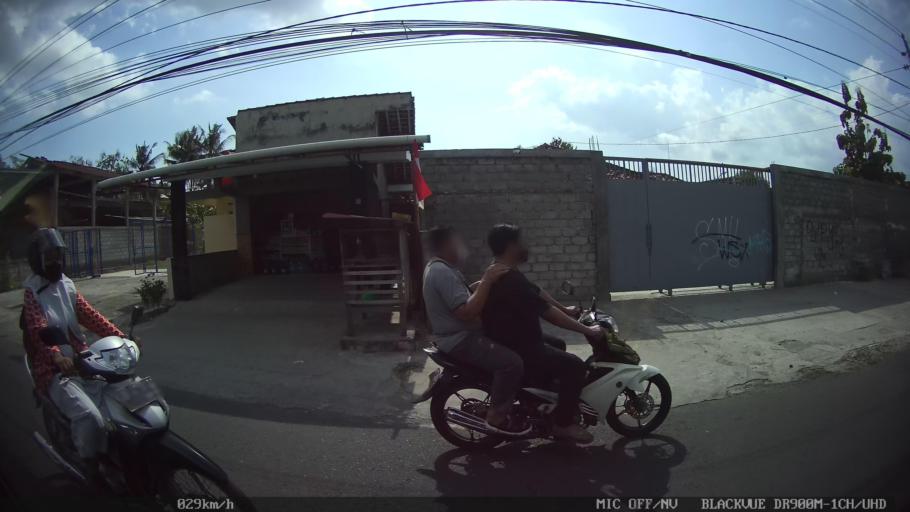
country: ID
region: Daerah Istimewa Yogyakarta
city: Kasihan
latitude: -7.8333
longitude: 110.3137
